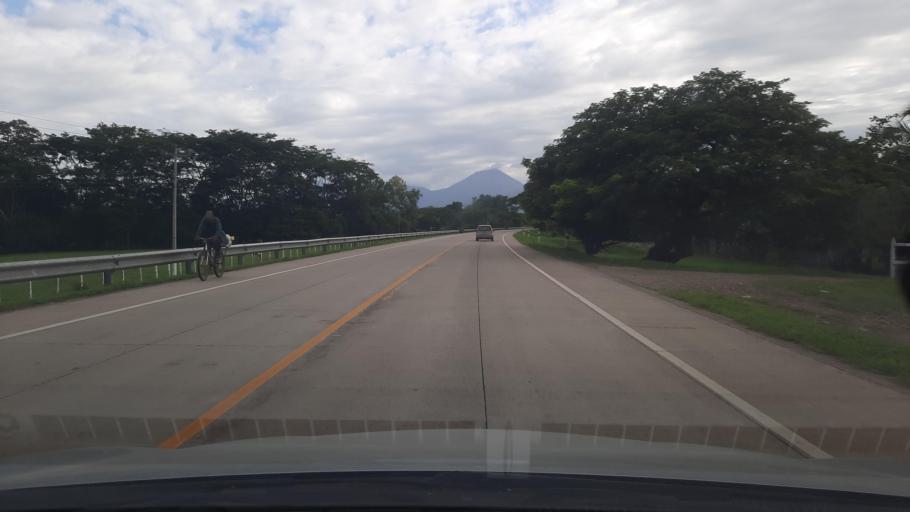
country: NI
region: Chinandega
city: Somotillo
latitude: 12.8431
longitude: -86.8801
